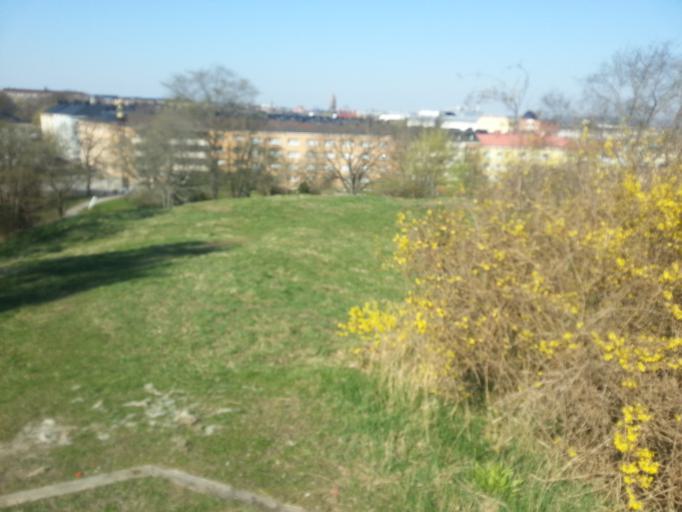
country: SE
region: OEstergoetland
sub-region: Norrkopings Kommun
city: Norrkoping
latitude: 58.5890
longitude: 16.2043
